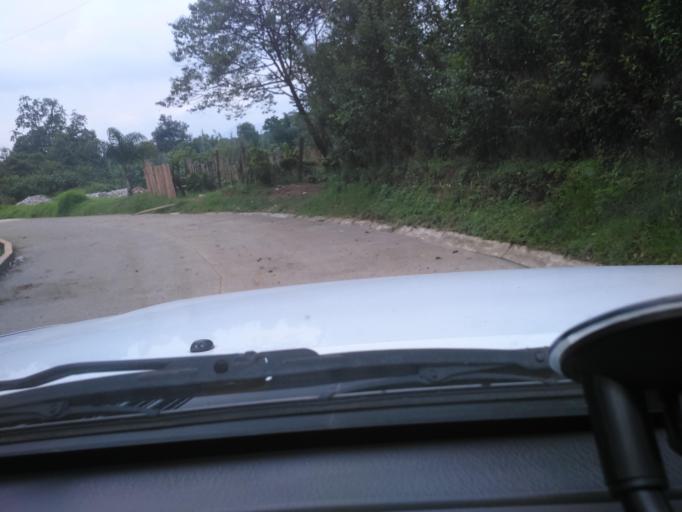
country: MX
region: Veracruz
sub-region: Mariano Escobedo
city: Chicola
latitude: 18.9123
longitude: -97.1103
